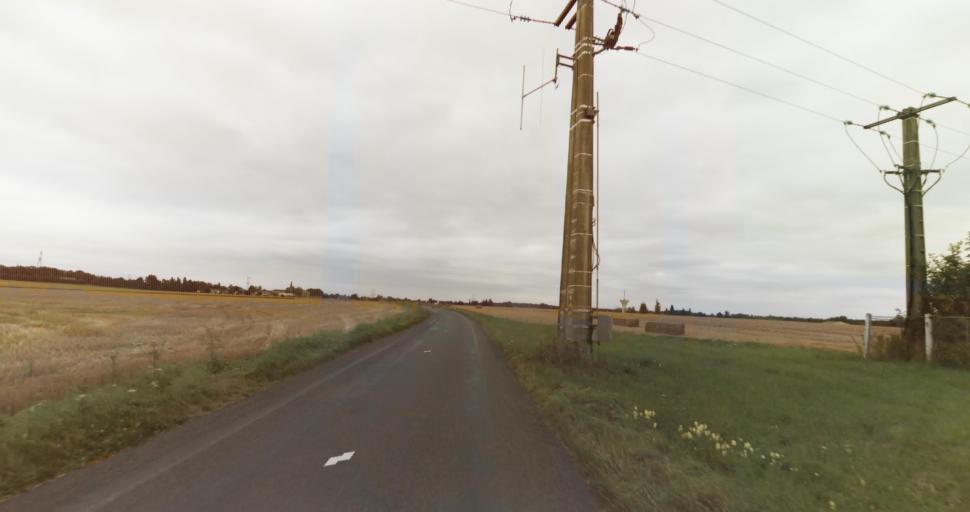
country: FR
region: Haute-Normandie
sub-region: Departement de l'Eure
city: La Couture-Boussey
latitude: 48.9053
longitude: 1.4074
